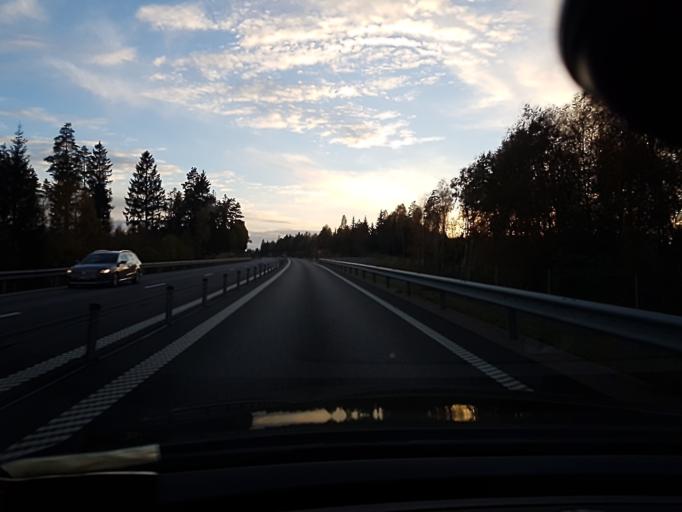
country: SE
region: Kronoberg
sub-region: Ljungby Kommun
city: Ljungby
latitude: 56.7857
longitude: 13.8274
